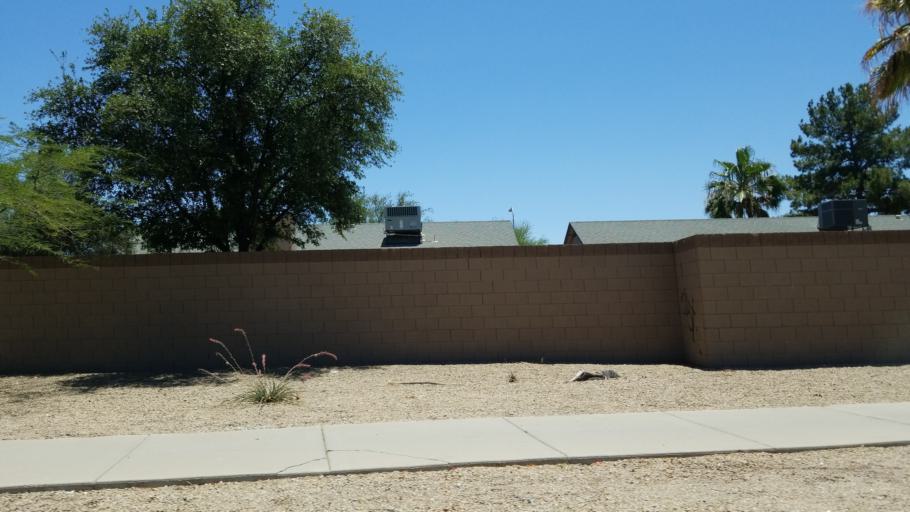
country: US
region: Arizona
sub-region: Maricopa County
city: Tolleson
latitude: 33.5087
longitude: -112.2436
